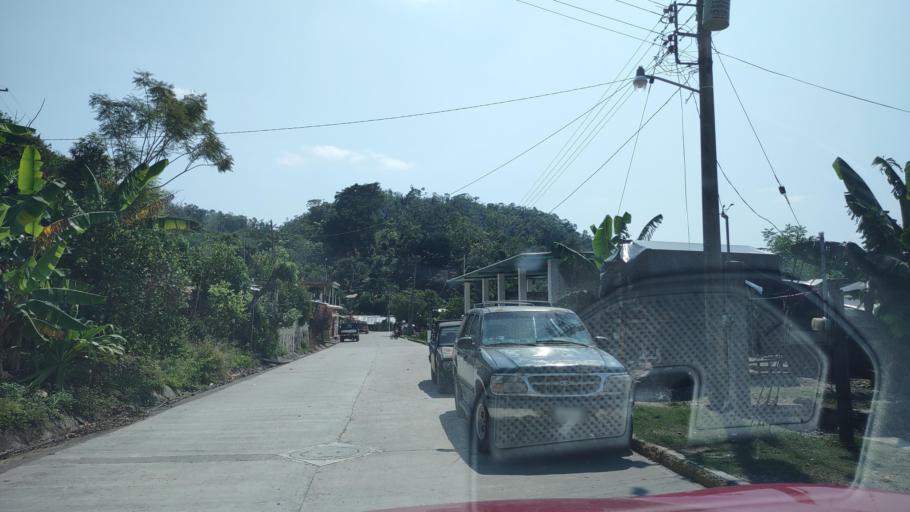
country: MX
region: Veracruz
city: Agua Dulce
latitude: 20.3111
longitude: -97.1713
